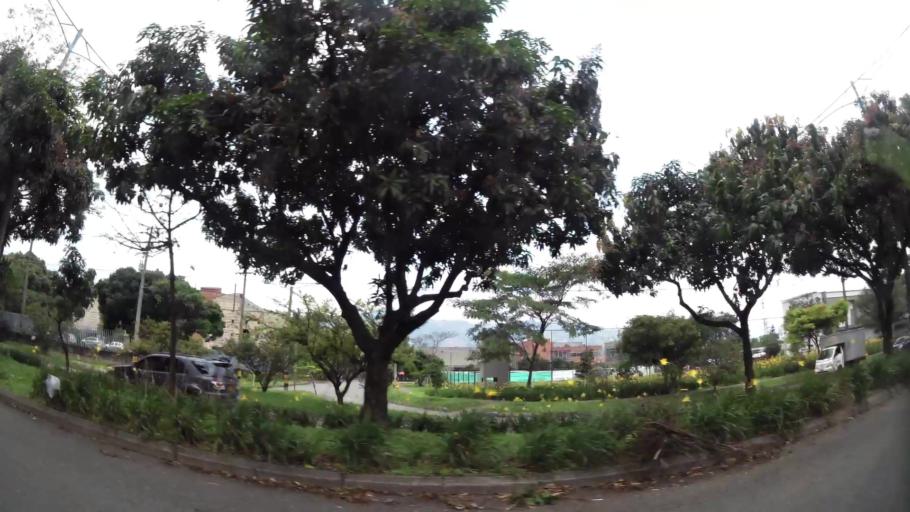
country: CO
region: Antioquia
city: Envigado
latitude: 6.1678
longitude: -75.5979
